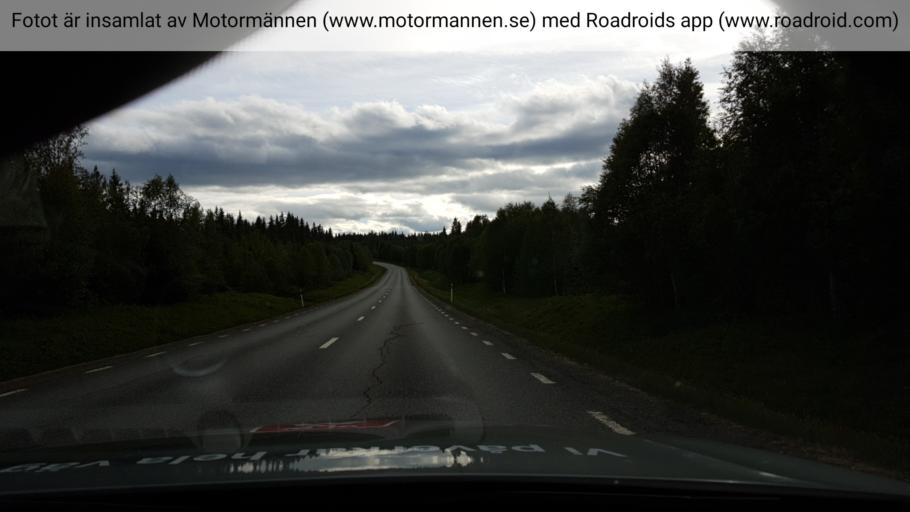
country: SE
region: Jaemtland
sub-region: OEstersunds Kommun
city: Lit
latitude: 63.4722
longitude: 15.1995
